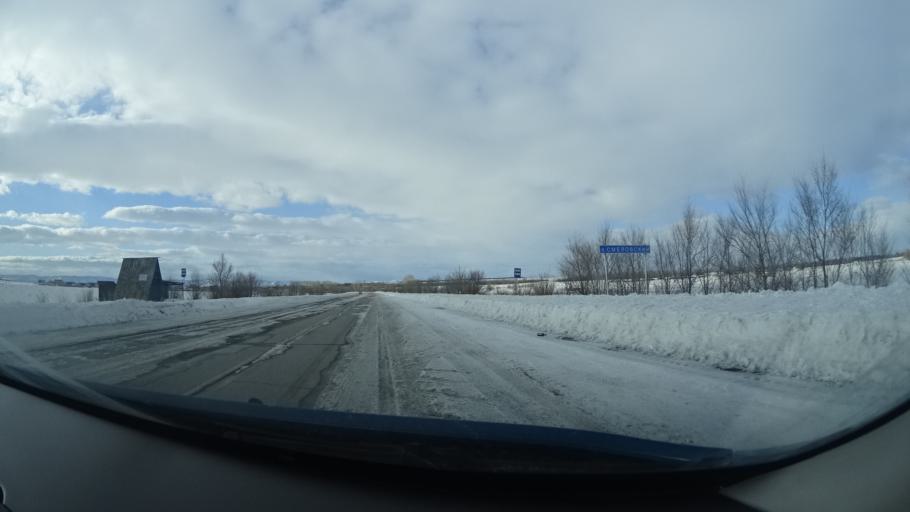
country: RU
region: Chelyabinsk
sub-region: Gorod Magnitogorsk
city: Magnitogorsk
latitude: 53.5876
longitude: 58.8798
